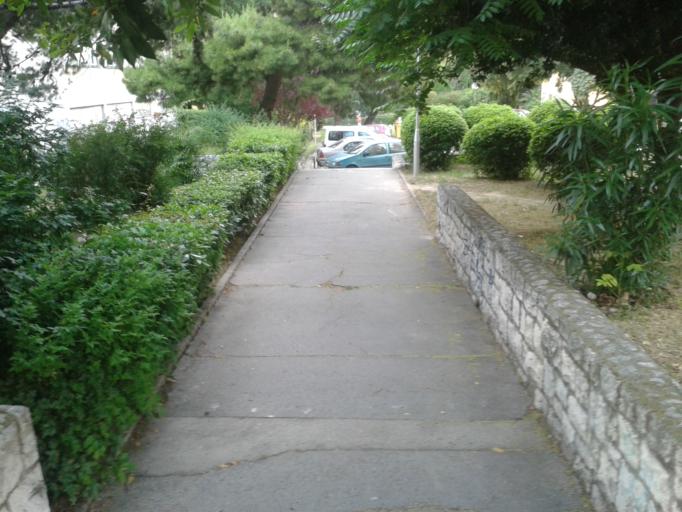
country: HR
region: Splitsko-Dalmatinska
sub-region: Grad Split
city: Split
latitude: 43.5133
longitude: 16.4498
